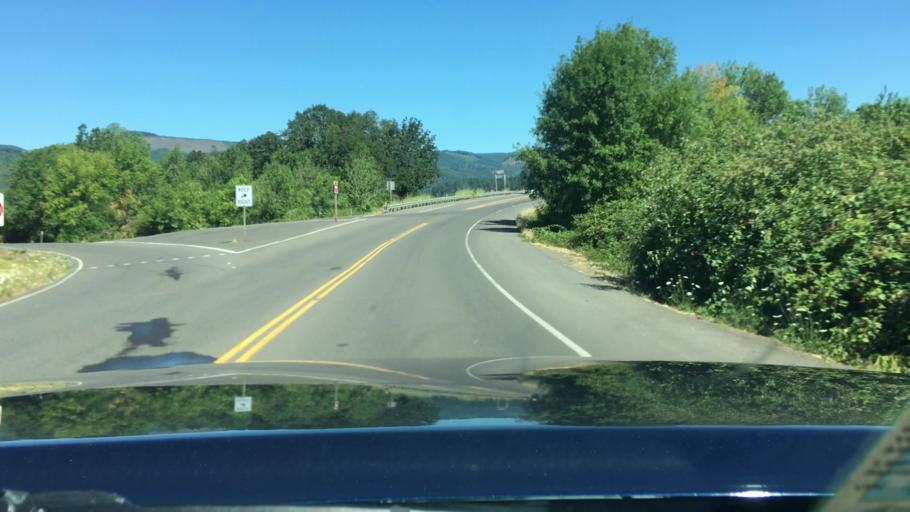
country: US
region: Oregon
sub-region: Lane County
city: Cottage Grove
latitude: 43.8327
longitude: -123.0330
